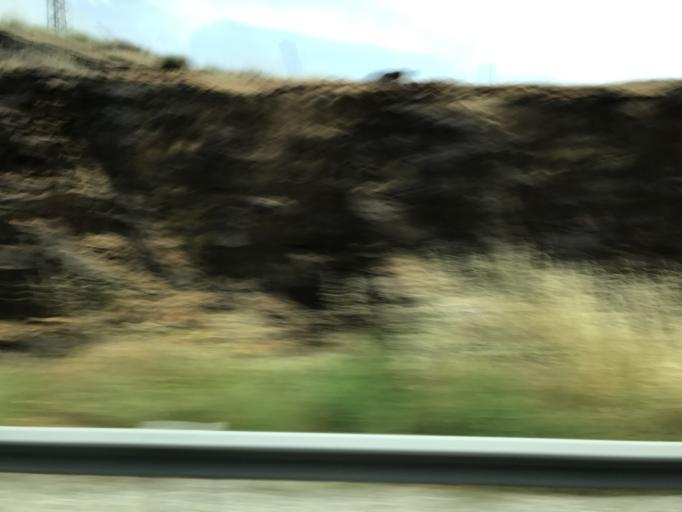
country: ES
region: Madrid
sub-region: Provincia de Madrid
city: Buitrago del Lozoya
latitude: 40.9877
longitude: -3.6415
